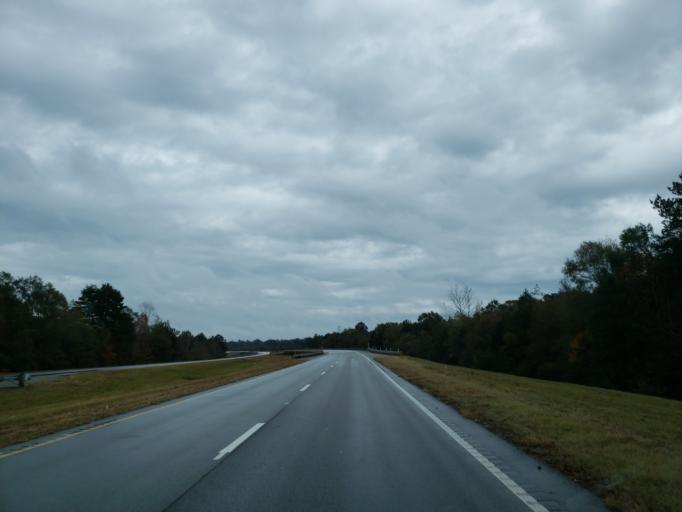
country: US
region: Mississippi
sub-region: Wayne County
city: Waynesboro
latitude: 31.6824
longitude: -88.6822
